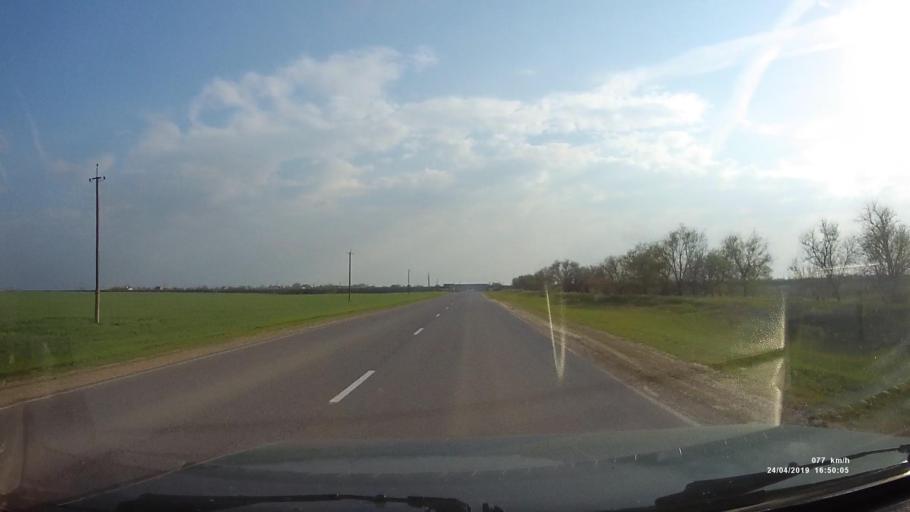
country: RU
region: Rostov
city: Proletarsk
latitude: 46.7091
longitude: 41.7574
